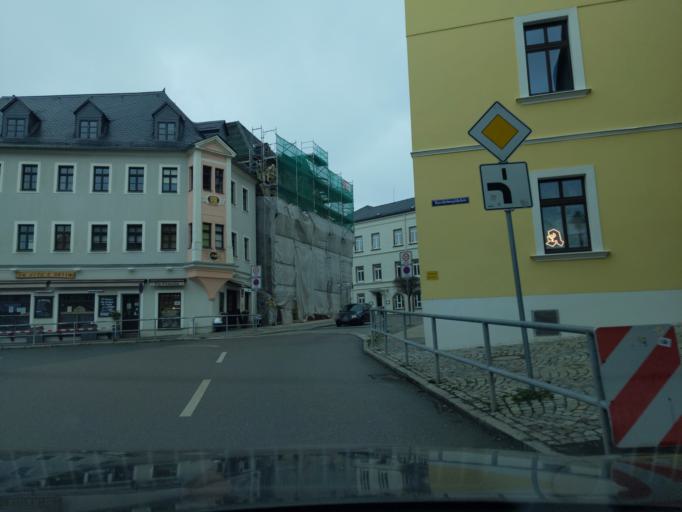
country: DE
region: Saxony
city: Schneeberg
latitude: 50.5949
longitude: 12.6406
